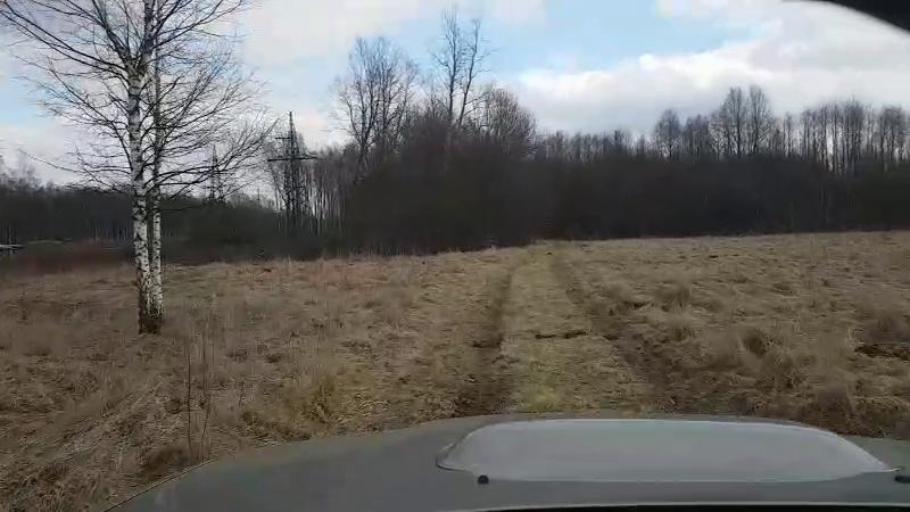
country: EE
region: Jaervamaa
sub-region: Paide linn
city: Paide
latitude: 58.8764
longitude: 25.5358
